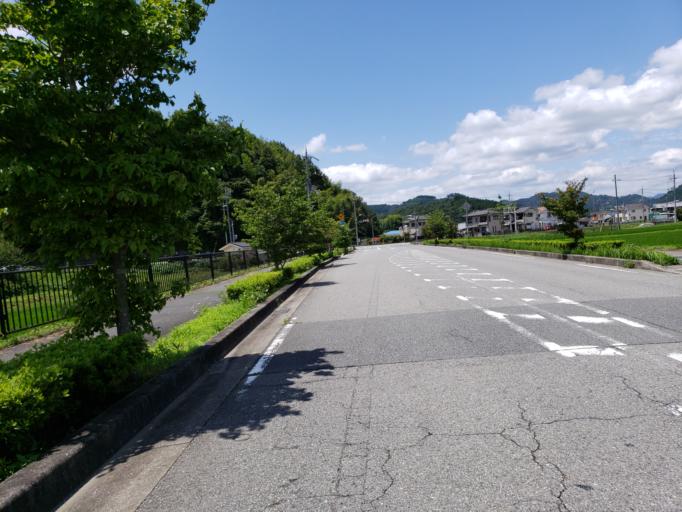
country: JP
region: Hyogo
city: Himeji
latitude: 34.9300
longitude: 134.7294
